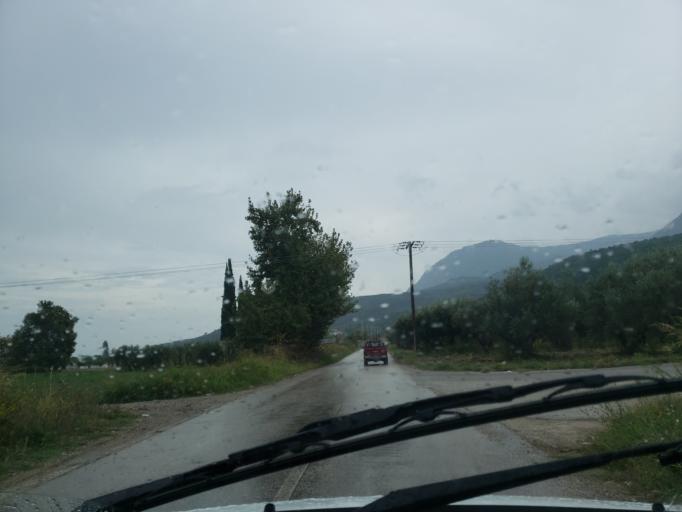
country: GR
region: Central Greece
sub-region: Nomos Fthiotidos
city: Anthili
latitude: 38.7999
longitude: 22.4652
